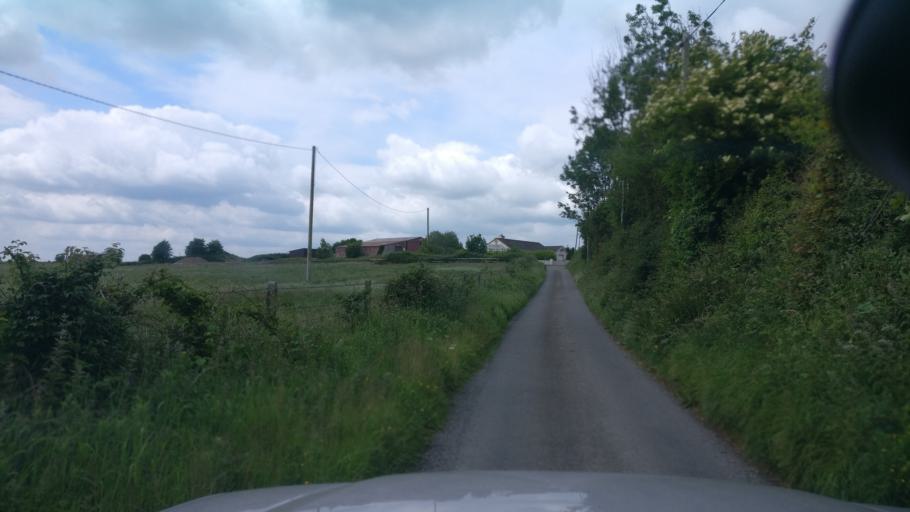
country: IE
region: Connaught
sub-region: County Galway
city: Ballinasloe
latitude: 53.2876
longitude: -8.3163
